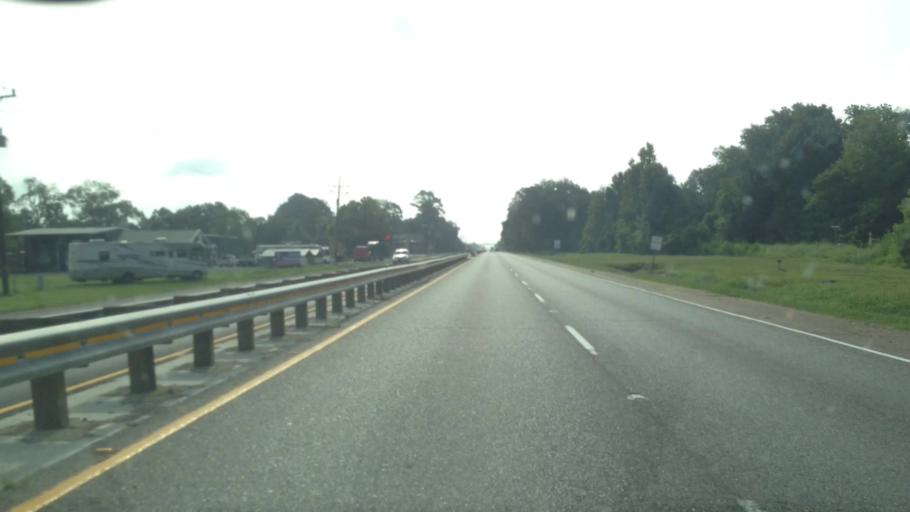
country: US
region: Louisiana
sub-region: Pointe Coupee Parish
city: Livonia
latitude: 30.5550
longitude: -91.5695
